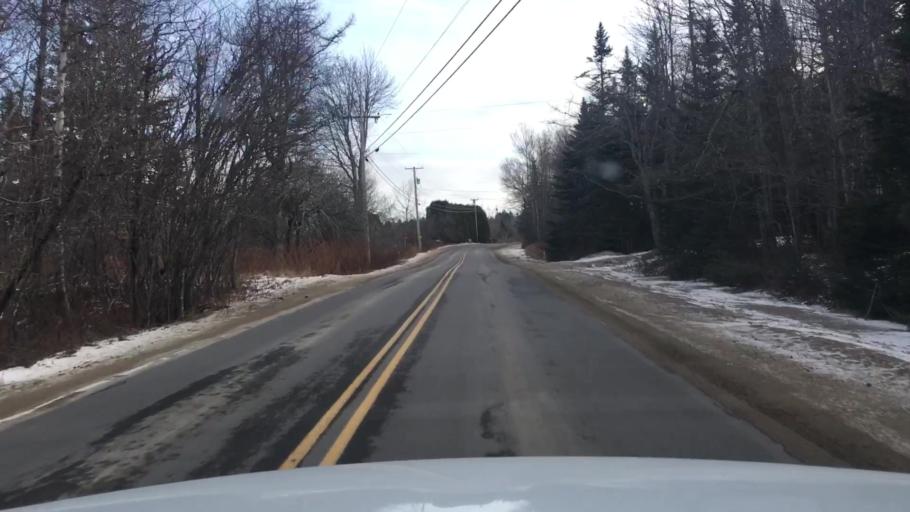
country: US
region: Maine
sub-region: Washington County
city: Jonesport
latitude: 44.6146
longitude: -67.6038
